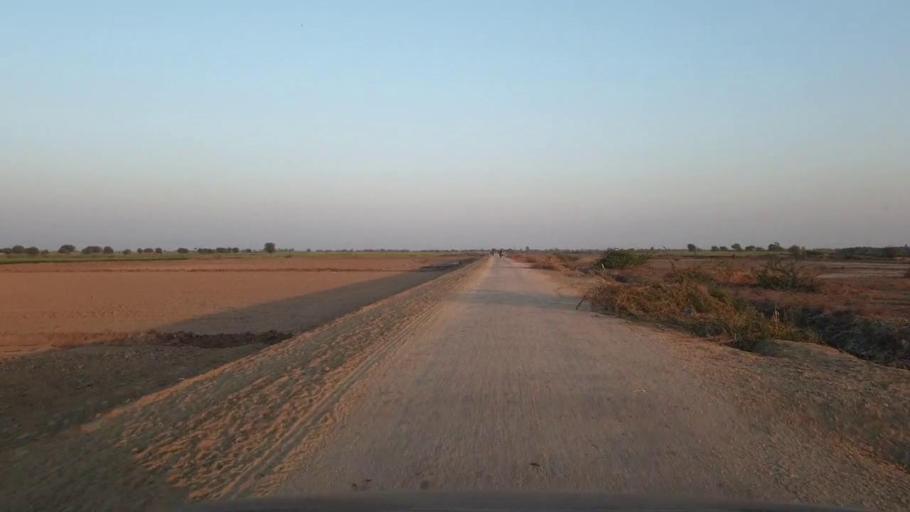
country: PK
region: Sindh
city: Digri
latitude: 25.1407
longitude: 69.2425
